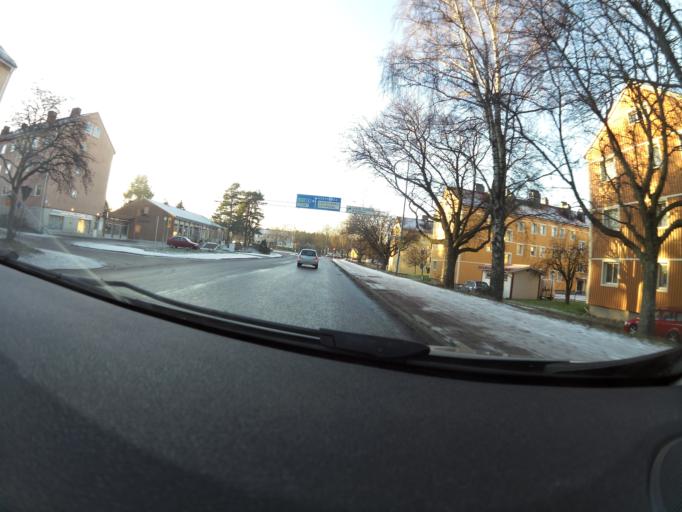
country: SE
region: Gaevleborg
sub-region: Gavle Kommun
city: Gavle
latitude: 60.6647
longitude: 17.1407
